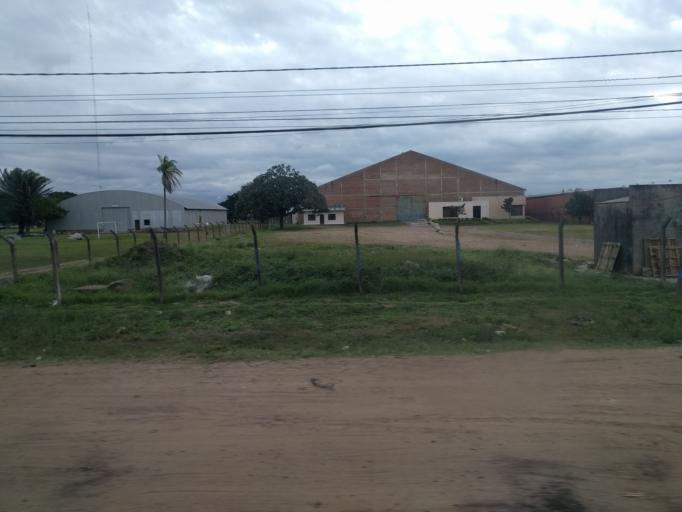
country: BO
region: Santa Cruz
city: Santa Cruz de la Sierra
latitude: -17.7067
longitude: -63.1600
